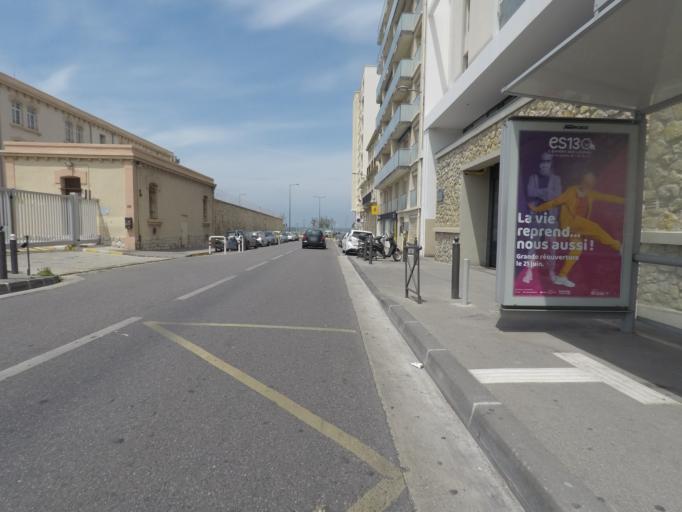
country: FR
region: Provence-Alpes-Cote d'Azur
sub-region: Departement des Bouches-du-Rhone
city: Marseille 07
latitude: 43.2896
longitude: 5.3571
